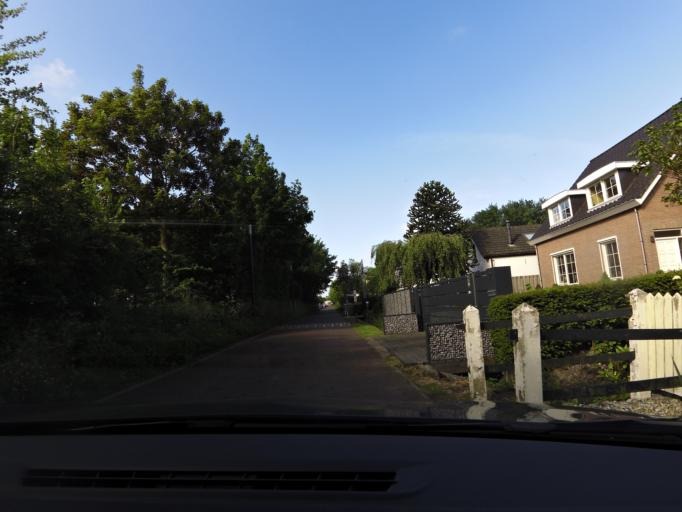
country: NL
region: Zeeland
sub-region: Schouwen-Duiveland
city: Renesse
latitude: 51.7353
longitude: 3.7775
